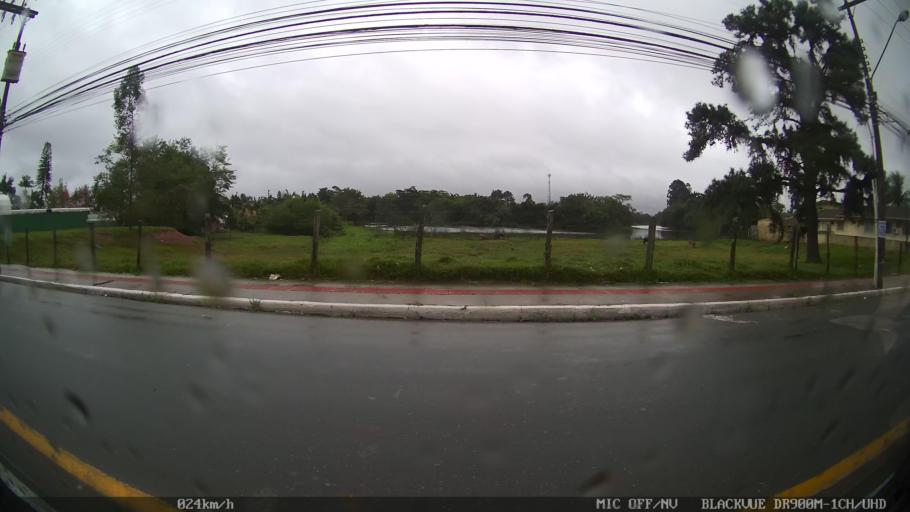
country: BR
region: Santa Catarina
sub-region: Itajai
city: Itajai
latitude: -26.9239
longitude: -48.6826
